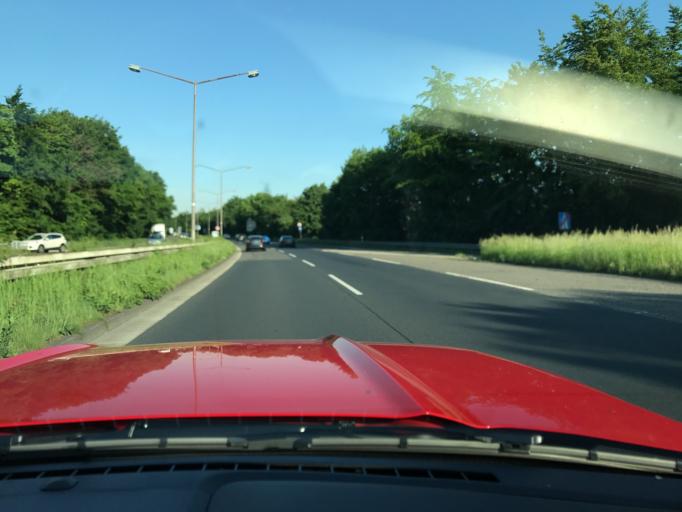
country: DE
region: North Rhine-Westphalia
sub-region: Regierungsbezirk Koln
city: Leverkusen
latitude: 51.0248
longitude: 6.9413
